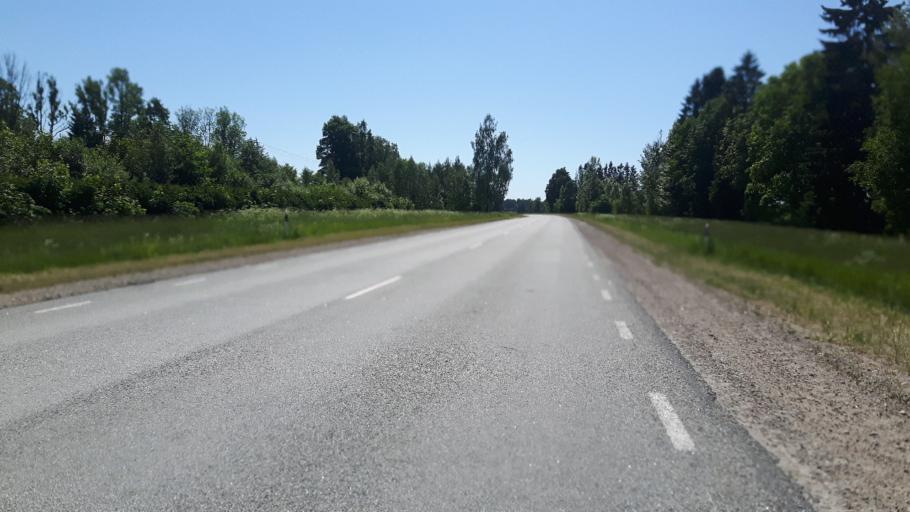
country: EE
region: Paernumaa
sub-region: Tootsi vald
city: Tootsi
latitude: 58.4640
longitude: 24.7839
